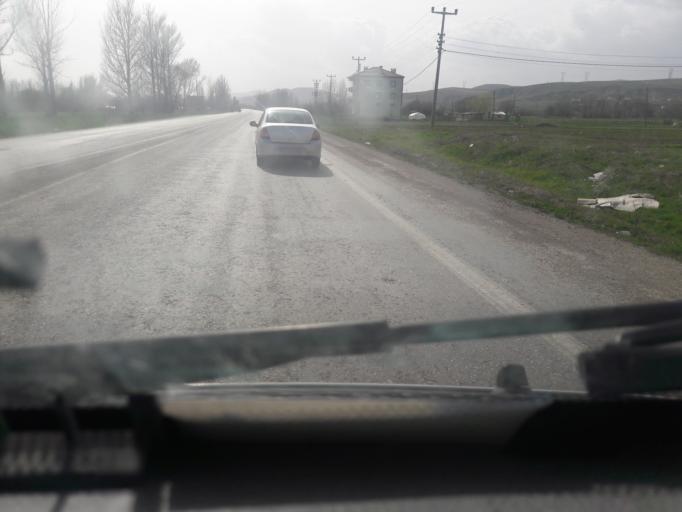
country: TR
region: Gumushane
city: Kelkit
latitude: 40.1429
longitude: 39.4306
